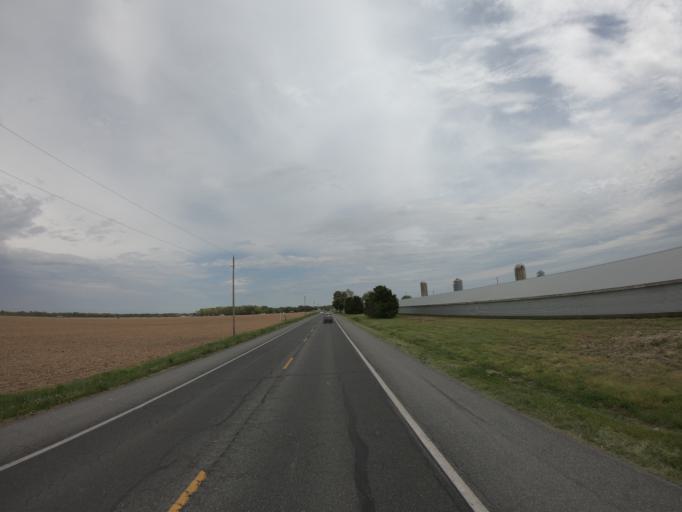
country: US
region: Delaware
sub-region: Sussex County
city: Milton
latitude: 38.7855
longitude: -75.3496
